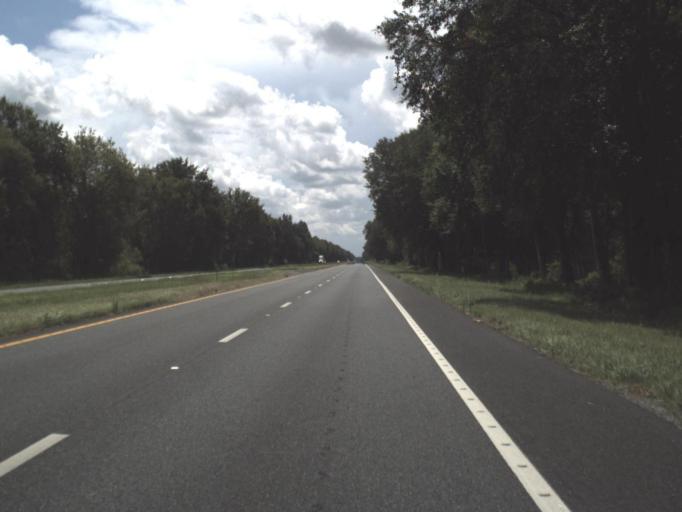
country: US
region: Florida
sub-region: Taylor County
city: Perry
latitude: 30.2238
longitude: -83.6762
